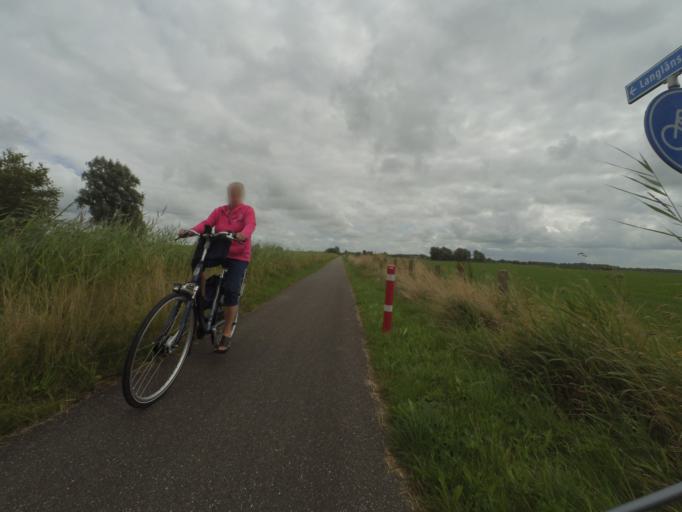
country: NL
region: Friesland
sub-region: Gemeente Kollumerland en Nieuwkruisland
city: Kollumerzwaag
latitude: 53.2958
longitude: 6.0995
